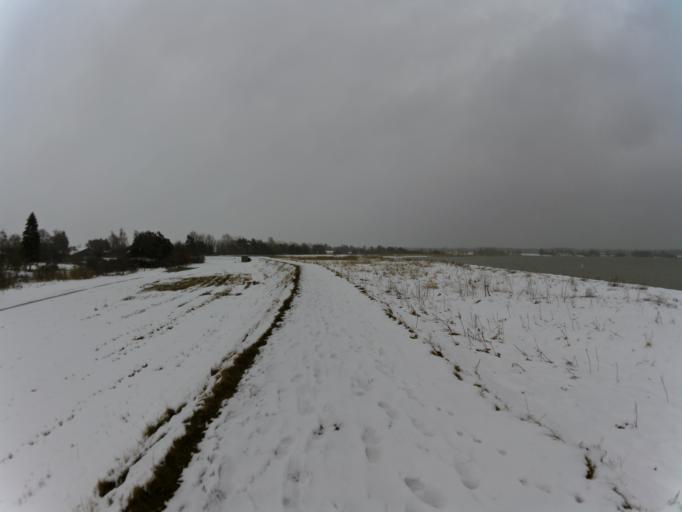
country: DK
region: Zealand
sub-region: Vordingborg Kommune
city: Neder Vindinge
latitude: 55.0486
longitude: 11.8329
